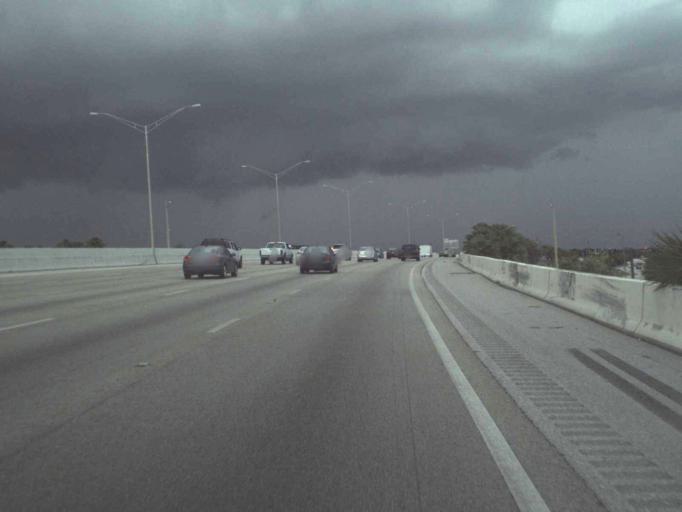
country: US
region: Florida
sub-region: Palm Beach County
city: Schall Circle
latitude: 26.7174
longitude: -80.0879
